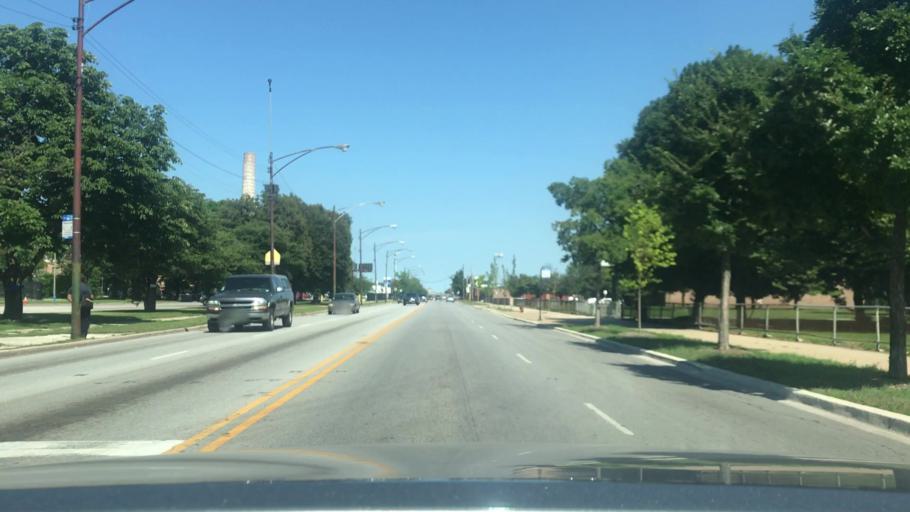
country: US
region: Illinois
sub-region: Cook County
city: Dolton
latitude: 41.7075
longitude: -87.6039
